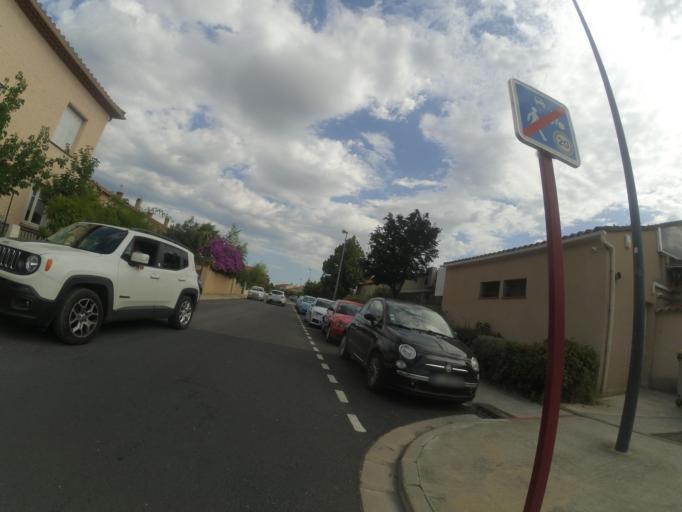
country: FR
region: Languedoc-Roussillon
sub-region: Departement des Pyrenees-Orientales
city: Toulouges
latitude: 42.6726
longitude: 2.8316
